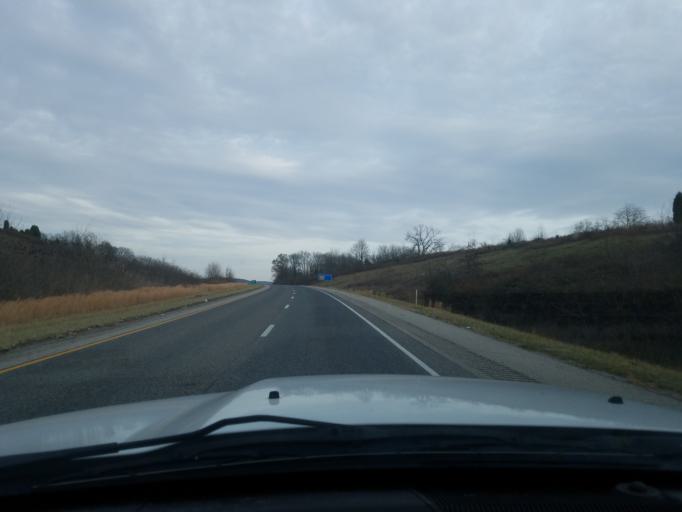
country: US
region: Indiana
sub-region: Dubois County
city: Ferdinand
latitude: 38.2167
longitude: -86.7284
